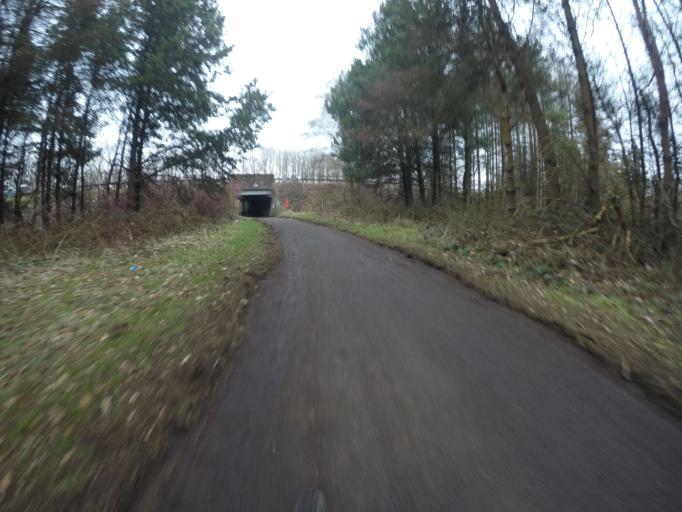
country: GB
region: Scotland
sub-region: North Ayrshire
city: Kilwinning
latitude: 55.6408
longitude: -4.6895
